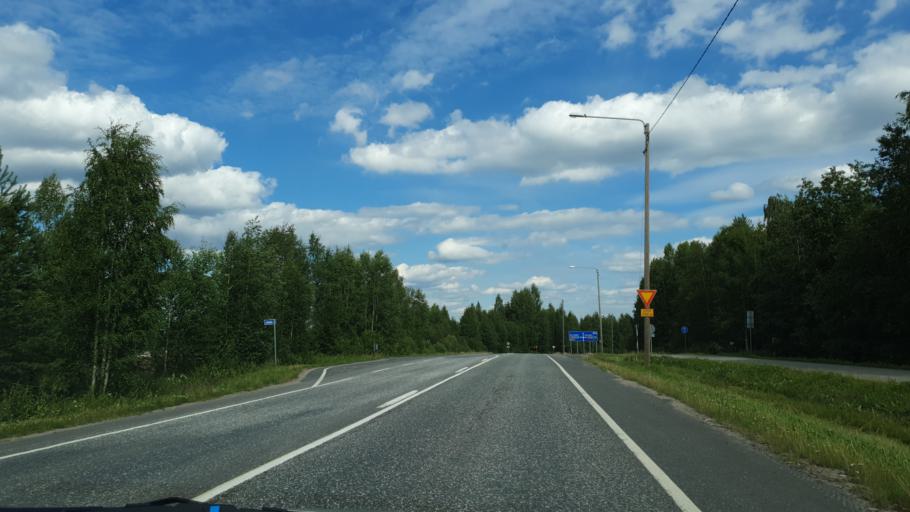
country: FI
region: Kainuu
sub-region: Kajaani
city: Kajaani
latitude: 64.2570
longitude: 27.8164
